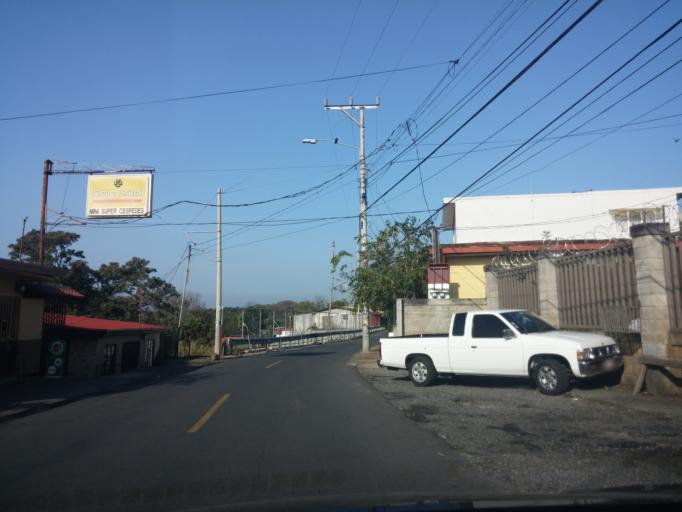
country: CR
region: Heredia
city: Mercedes
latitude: 10.0061
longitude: -84.1449
